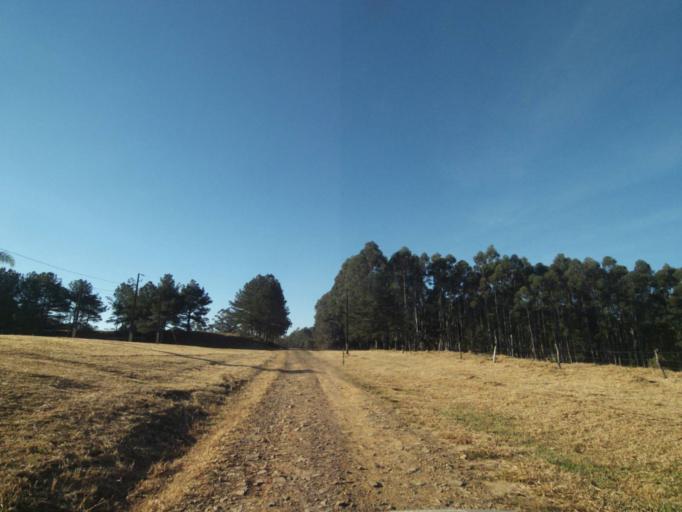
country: BR
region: Parana
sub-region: Telemaco Borba
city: Telemaco Borba
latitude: -24.5153
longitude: -50.6622
